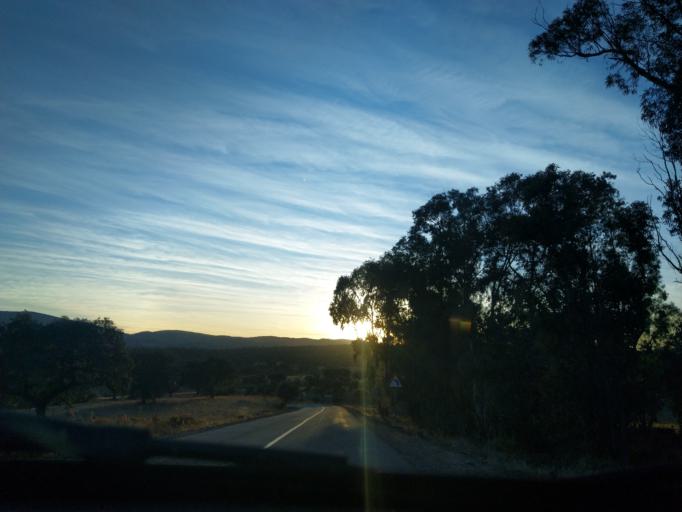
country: ES
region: Extremadura
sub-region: Provincia de Badajoz
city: Valverde de Llerena
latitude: 38.1822
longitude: -5.8638
